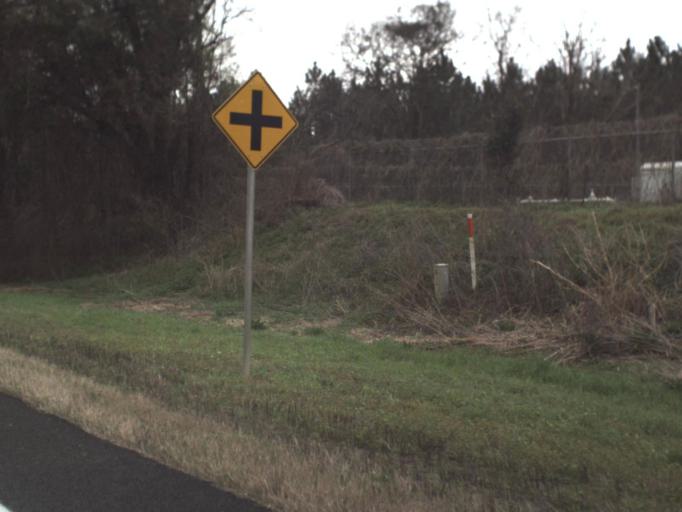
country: US
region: Florida
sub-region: Jefferson County
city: Monticello
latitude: 30.3856
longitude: -83.8331
